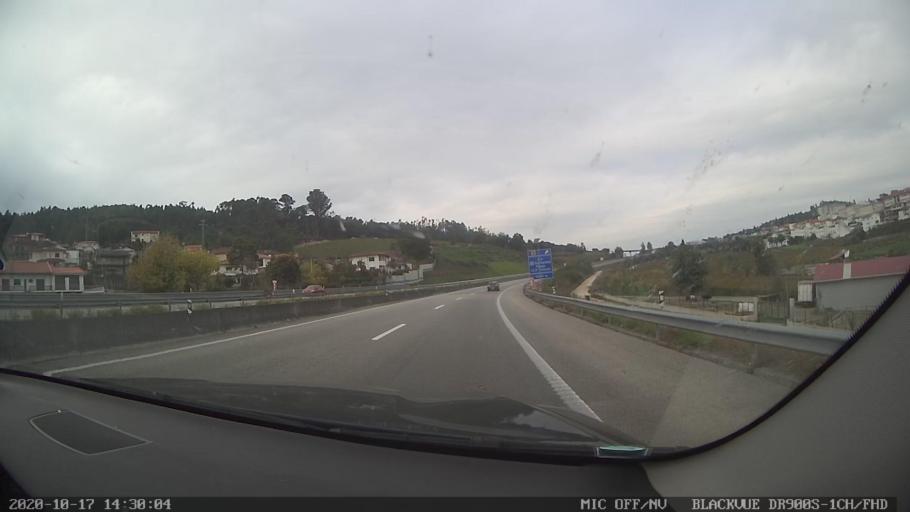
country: PT
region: Braga
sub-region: Guimaraes
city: Candoso
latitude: 41.4099
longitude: -8.3186
